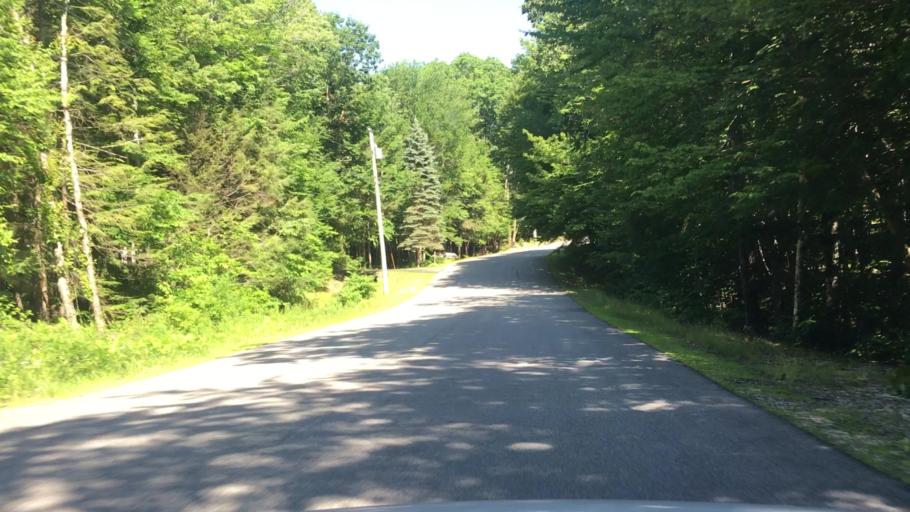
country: US
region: Maine
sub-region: Cumberland County
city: Cumberland Center
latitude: 43.8014
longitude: -70.3345
